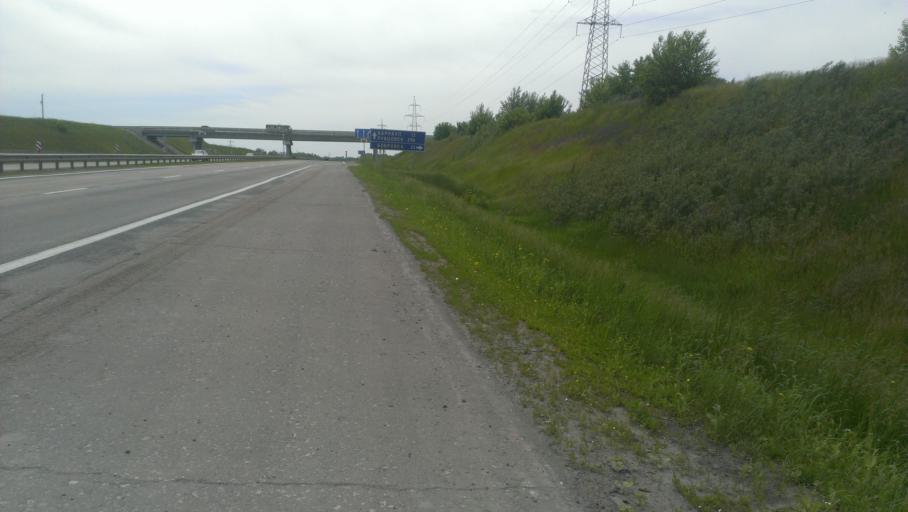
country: RU
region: Altai Krai
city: Sannikovo
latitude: 53.3422
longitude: 83.9383
